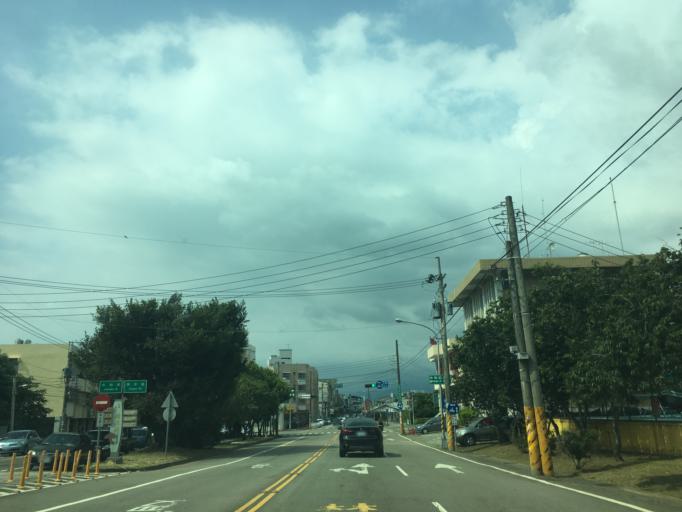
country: TW
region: Taiwan
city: Fengyuan
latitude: 24.2378
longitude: 120.8062
